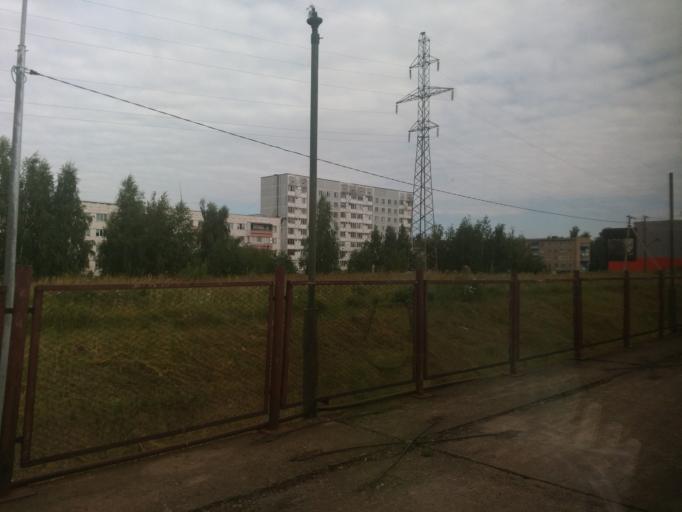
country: RU
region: Tatarstan
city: Mendeleyevsk
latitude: 55.8847
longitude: 52.3116
